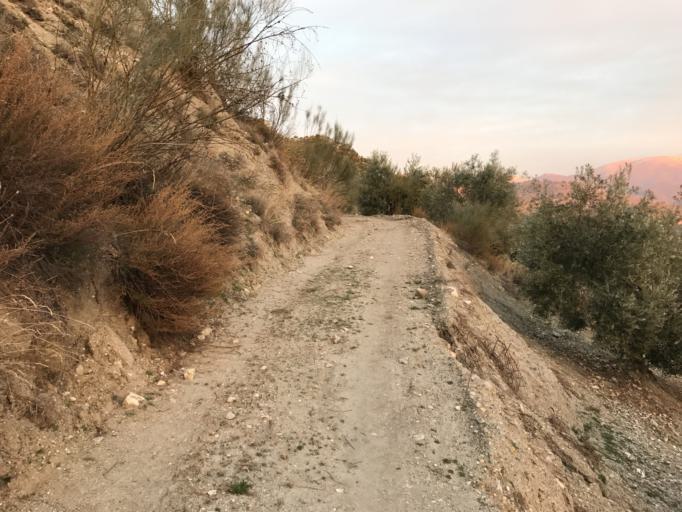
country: ES
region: Andalusia
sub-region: Provincia de Granada
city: Beas de Granada
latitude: 37.2085
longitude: -3.4906
